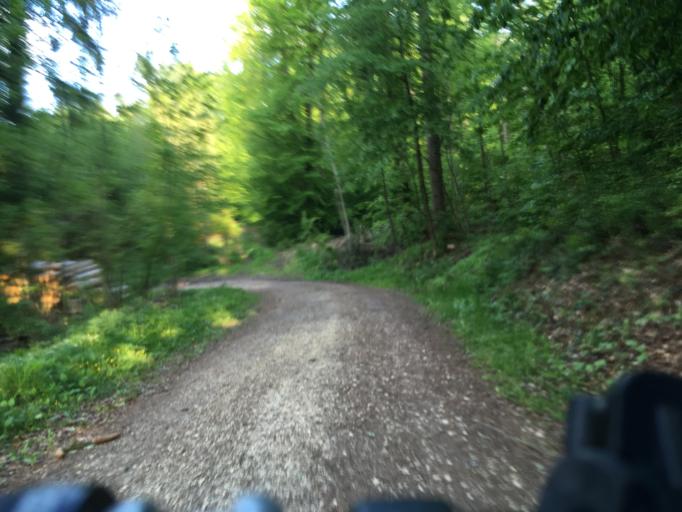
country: DE
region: Baden-Wuerttemberg
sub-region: Freiburg Region
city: Gailingen
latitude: 47.7043
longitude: 8.7596
